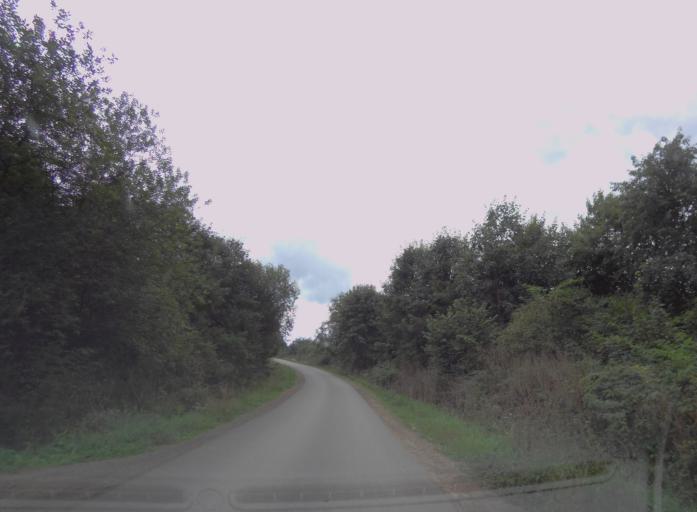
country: PL
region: Subcarpathian Voivodeship
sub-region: Powiat leski
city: Polanczyk
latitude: 49.3133
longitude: 22.5076
